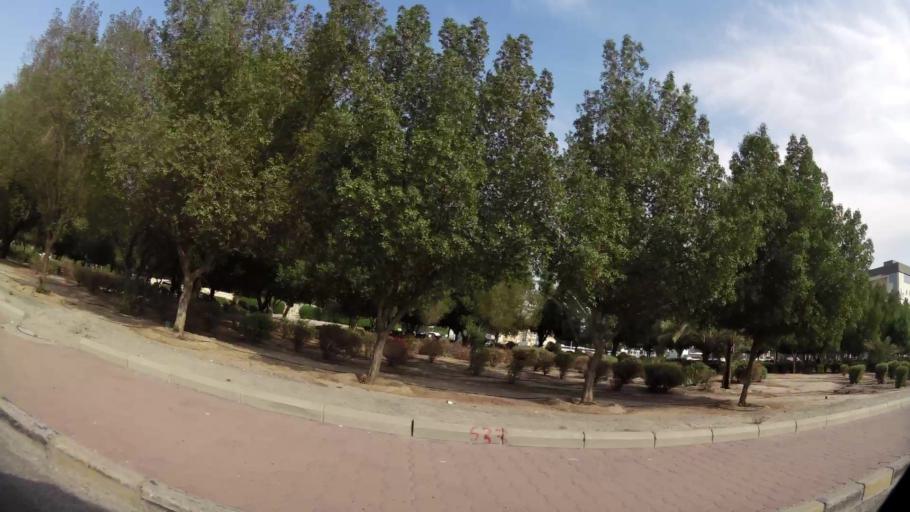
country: KW
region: Al Farwaniyah
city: Al Farwaniyah
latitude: 29.2969
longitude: 47.9649
